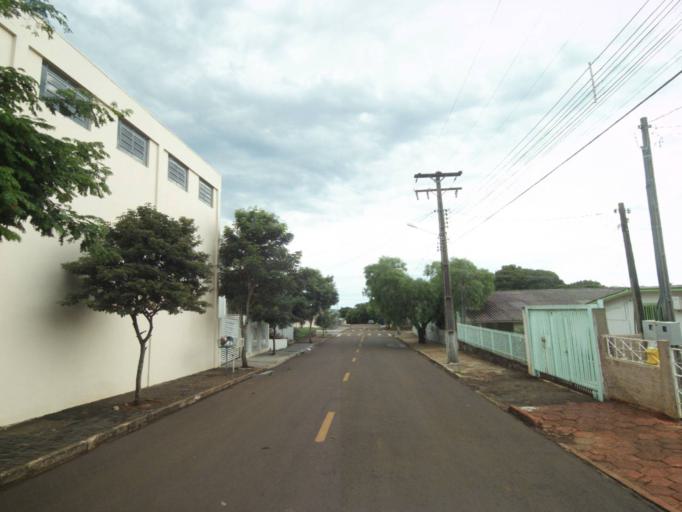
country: BR
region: Parana
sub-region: Guaraniacu
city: Guaraniacu
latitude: -25.1020
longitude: -52.8696
